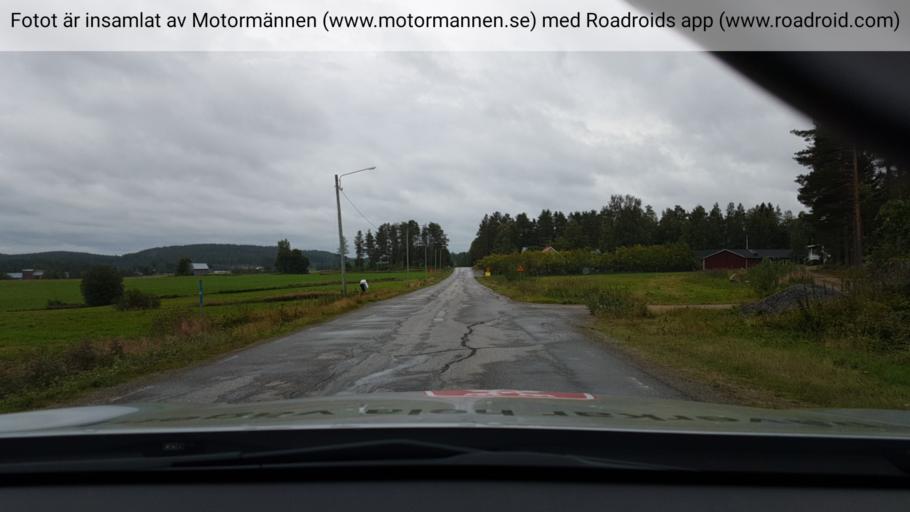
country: SE
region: Vaesterbotten
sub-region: Robertsfors Kommun
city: Robertsfors
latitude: 64.2498
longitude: 20.6592
